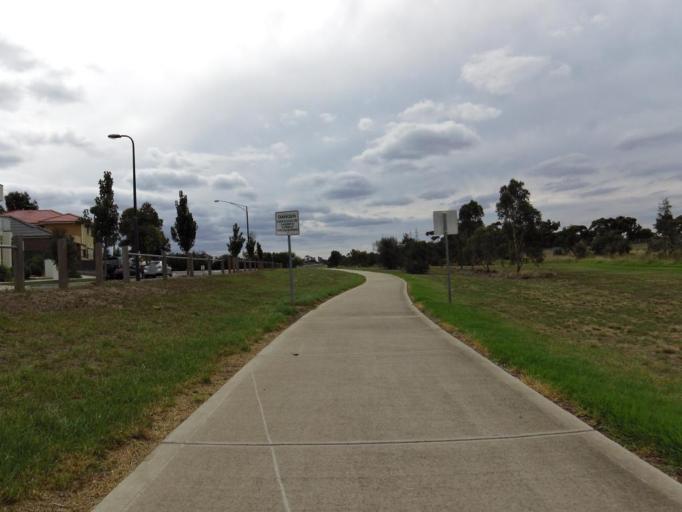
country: AU
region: Victoria
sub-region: Brimbank
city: St Albans
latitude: -37.7529
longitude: 144.7951
